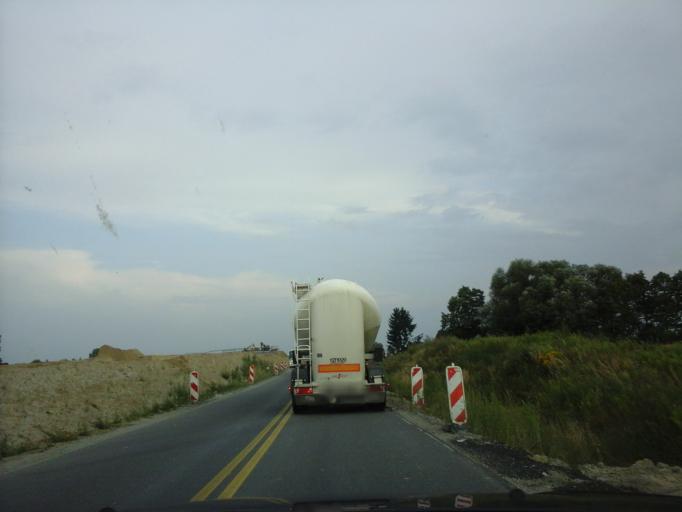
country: PL
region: Lower Silesian Voivodeship
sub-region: Powiat trzebnicki
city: Zmigrod
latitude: 51.5127
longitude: 16.8915
